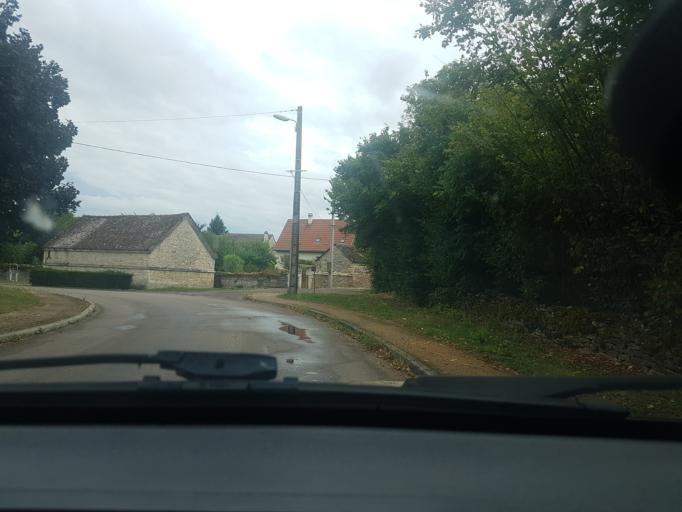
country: FR
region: Bourgogne
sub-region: Departement de Saone-et-Loire
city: Fontaines
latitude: 46.8591
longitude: 4.7622
